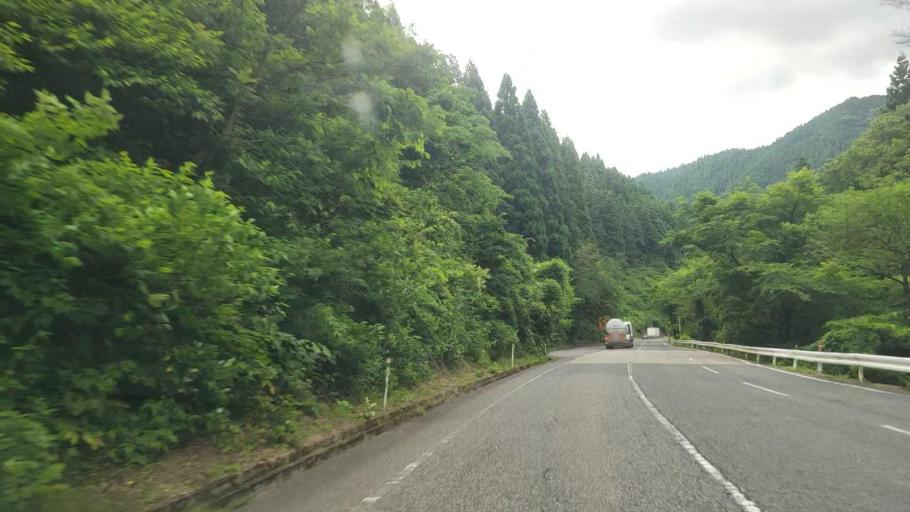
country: JP
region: Tottori
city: Yonago
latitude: 35.2594
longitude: 133.4377
